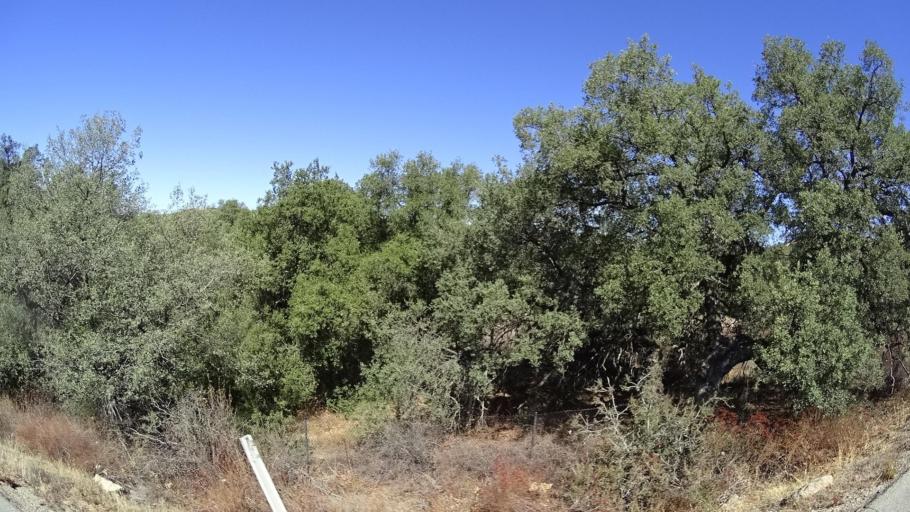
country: US
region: California
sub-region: San Diego County
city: Descanso
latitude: 32.7969
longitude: -116.6556
